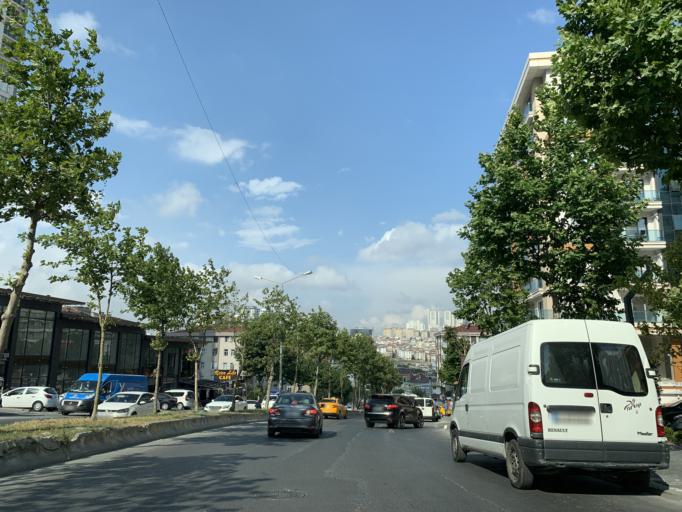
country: TR
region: Istanbul
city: Esenyurt
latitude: 41.0249
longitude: 28.6599
